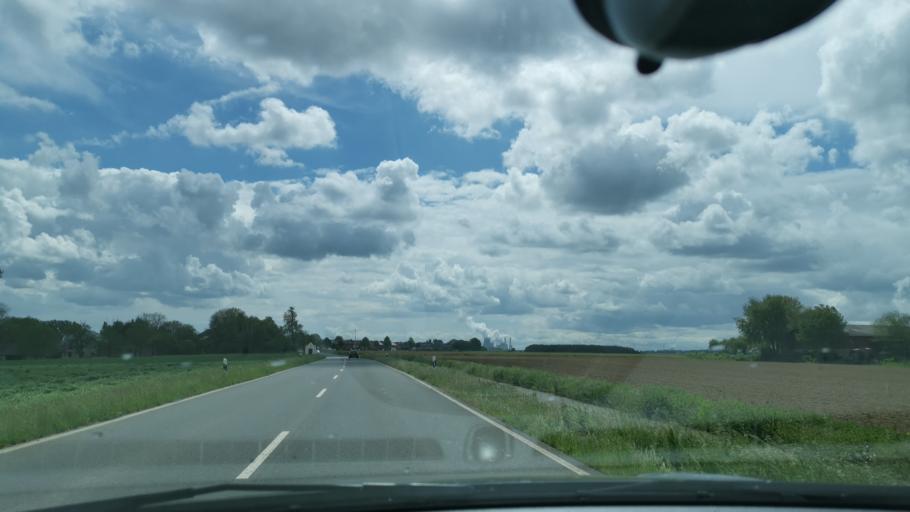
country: DE
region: North Rhine-Westphalia
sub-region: Regierungsbezirk Dusseldorf
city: Rommerskirchen
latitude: 51.0805
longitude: 6.6878
